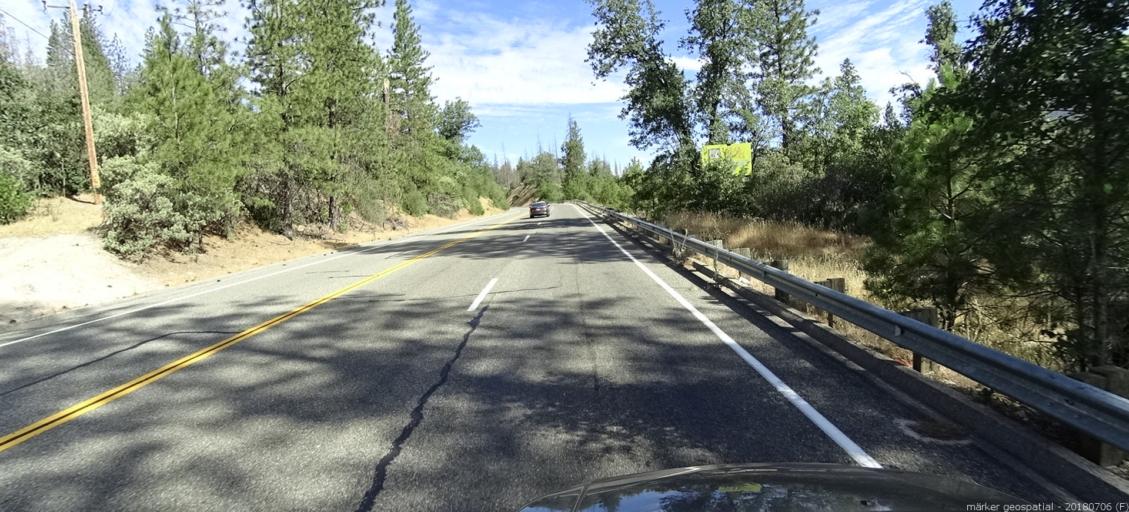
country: US
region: California
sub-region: Madera County
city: Oakhurst
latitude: 37.3399
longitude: -119.5863
